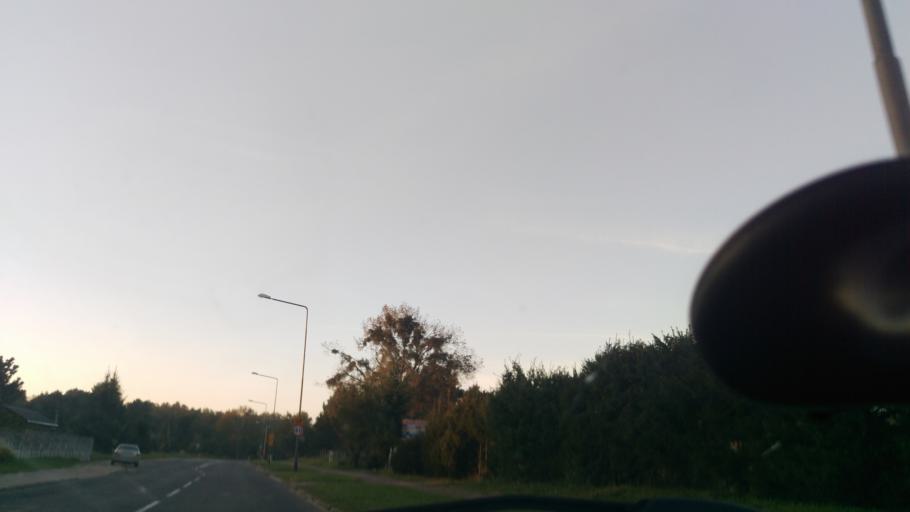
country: PL
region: West Pomeranian Voivodeship
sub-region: Powiat gryfinski
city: Stare Czarnowo
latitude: 53.3495
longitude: 14.7456
